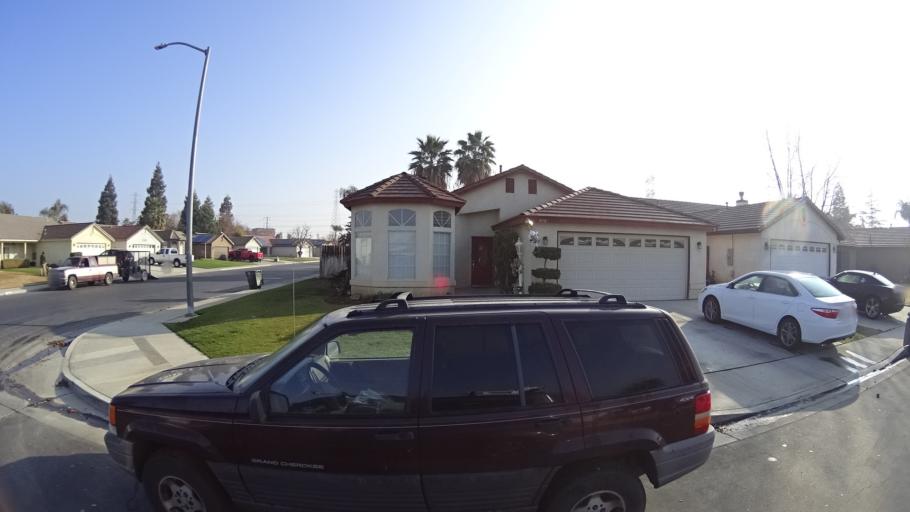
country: US
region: California
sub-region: Kern County
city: Greenacres
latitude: 35.3877
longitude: -119.0986
